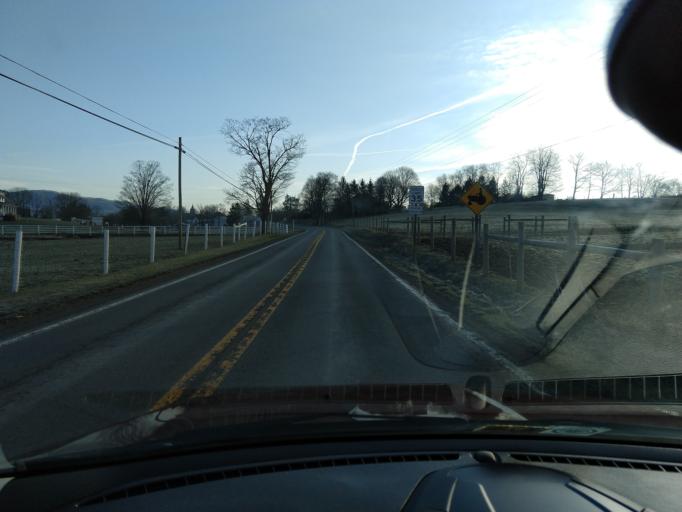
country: US
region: West Virginia
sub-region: Pocahontas County
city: Marlinton
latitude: 38.1323
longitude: -80.2170
